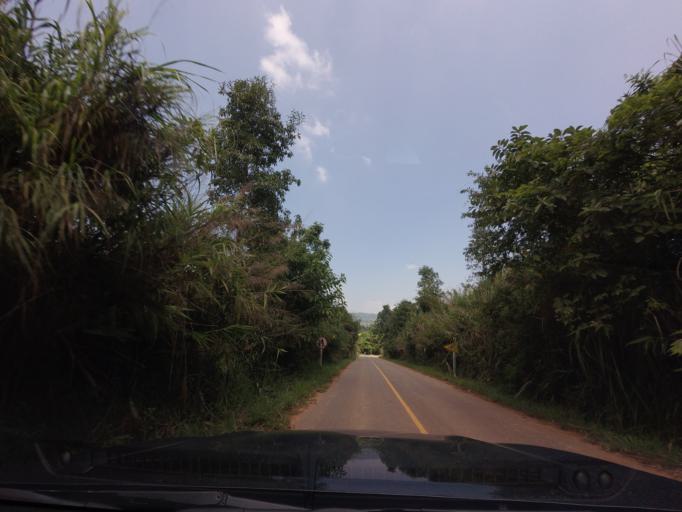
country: TH
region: Loei
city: Na Haeo
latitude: 17.5295
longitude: 100.8795
